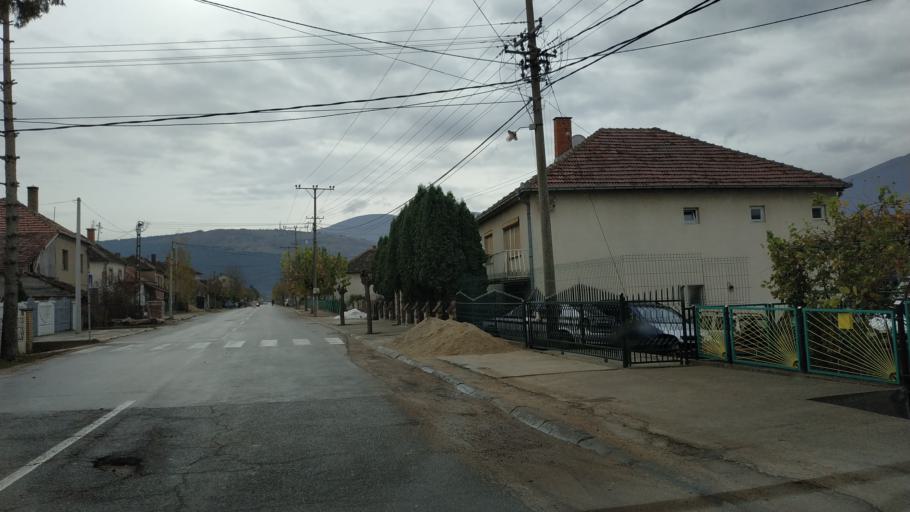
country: RS
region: Central Serbia
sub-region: Pirotski Okrug
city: Bela Palanka
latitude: 43.2292
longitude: 22.3172
